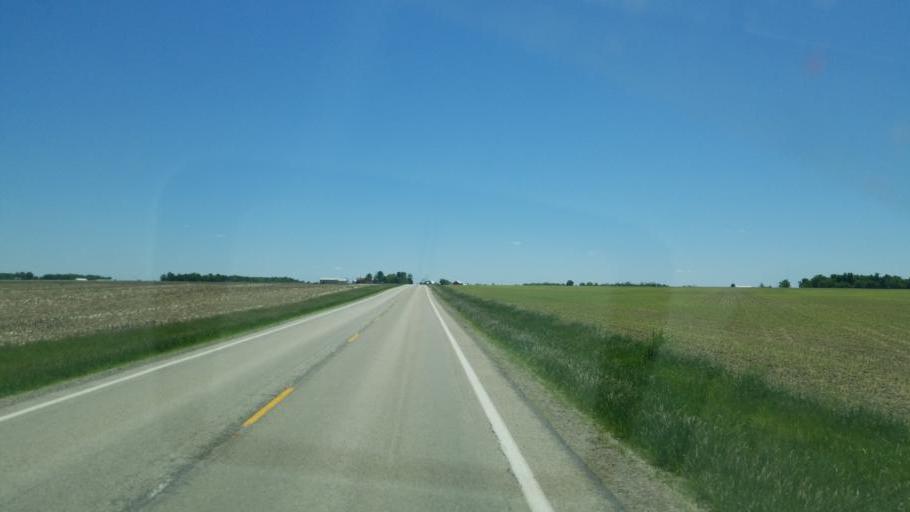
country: US
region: Ohio
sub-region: Darke County
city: Ansonia
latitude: 40.2744
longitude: -84.7060
